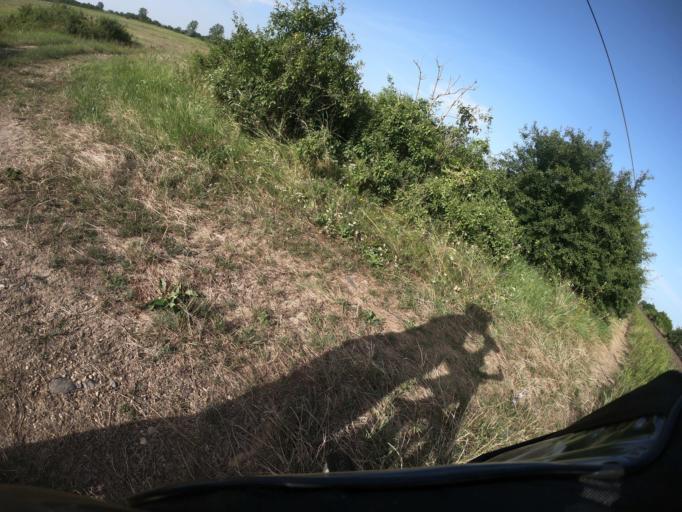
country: HU
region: Hajdu-Bihar
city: Tiszacsege
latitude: 47.6155
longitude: 21.0163
